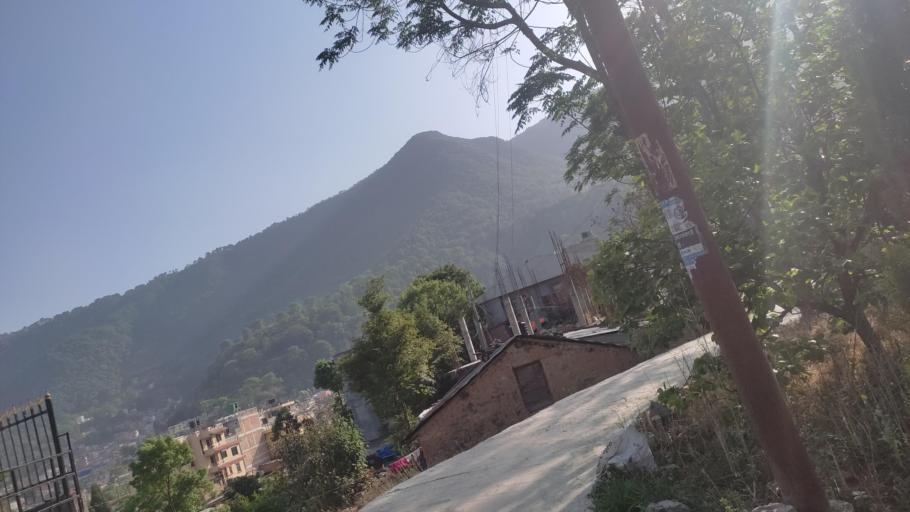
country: NP
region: Central Region
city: Kirtipur
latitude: 27.6509
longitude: 85.2810
